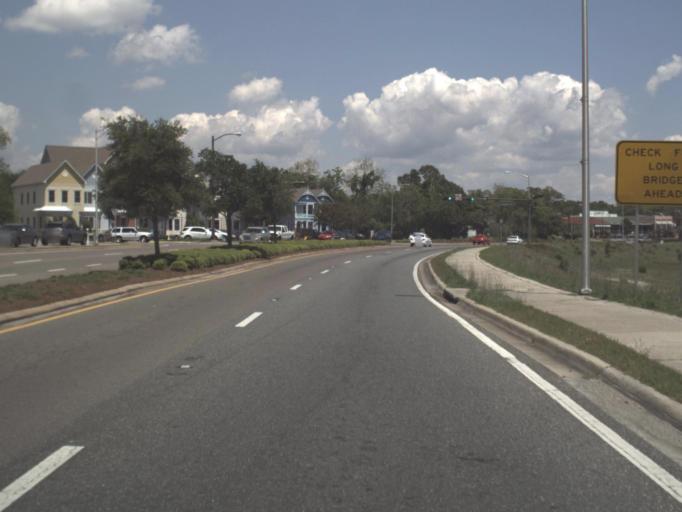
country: US
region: Florida
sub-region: Escambia County
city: Pensacola
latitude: 30.4159
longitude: -87.2002
